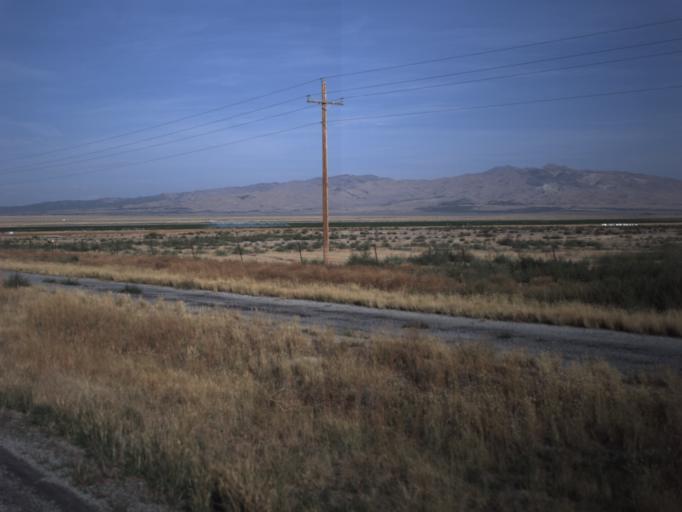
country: US
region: Idaho
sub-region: Oneida County
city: Malad City
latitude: 41.9664
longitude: -112.9281
